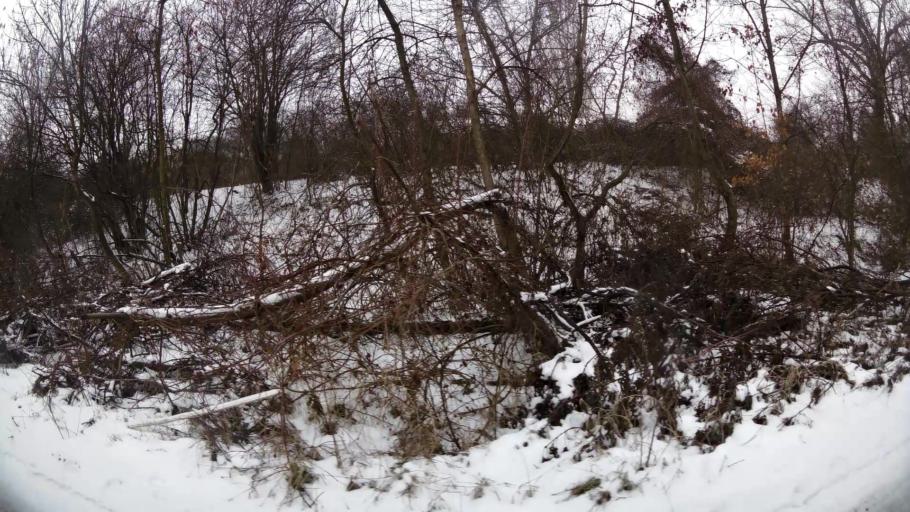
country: BG
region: Sofia-Capital
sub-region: Stolichna Obshtina
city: Sofia
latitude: 42.7175
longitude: 23.3030
